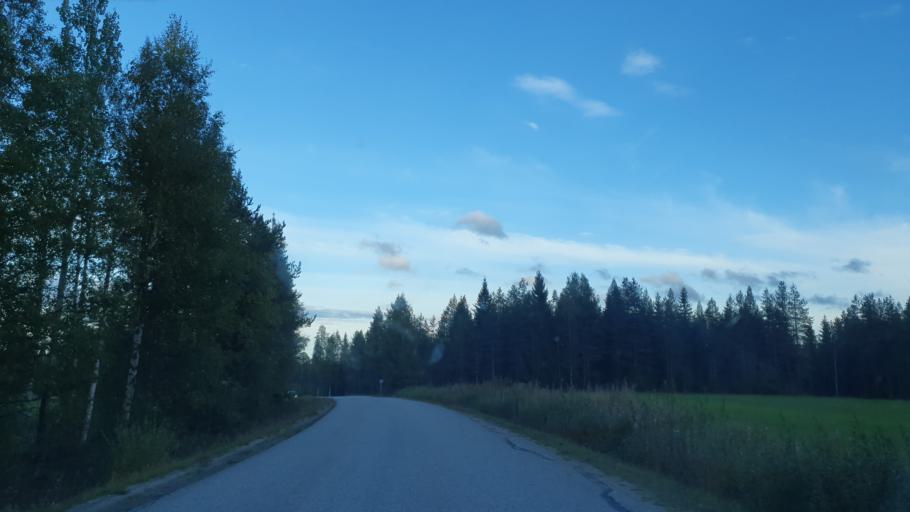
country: FI
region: Kainuu
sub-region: Kehys-Kainuu
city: Kuhmo
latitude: 64.4147
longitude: 29.9455
